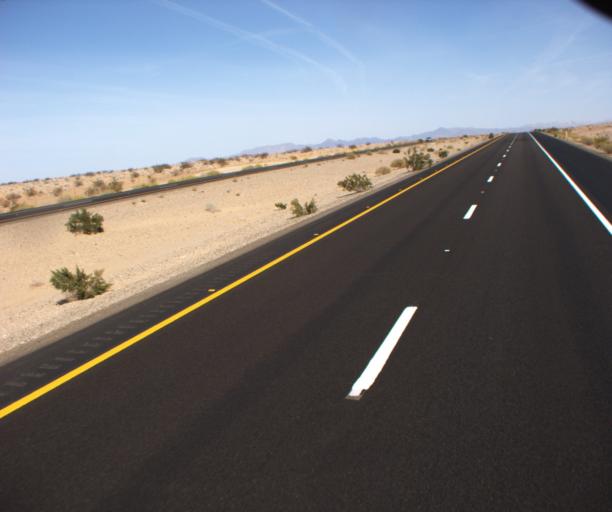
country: US
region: Arizona
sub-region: Yuma County
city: Somerton
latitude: 32.4951
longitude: -114.6133
